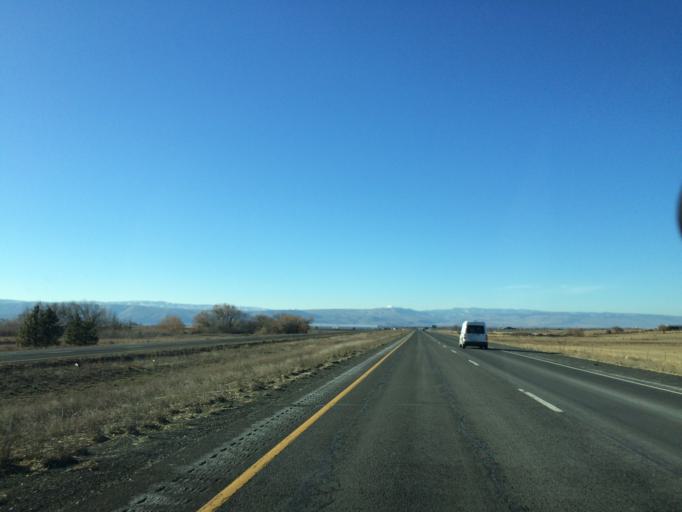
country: US
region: Washington
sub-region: Kittitas County
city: Kittitas
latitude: 46.9729
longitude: -120.3805
